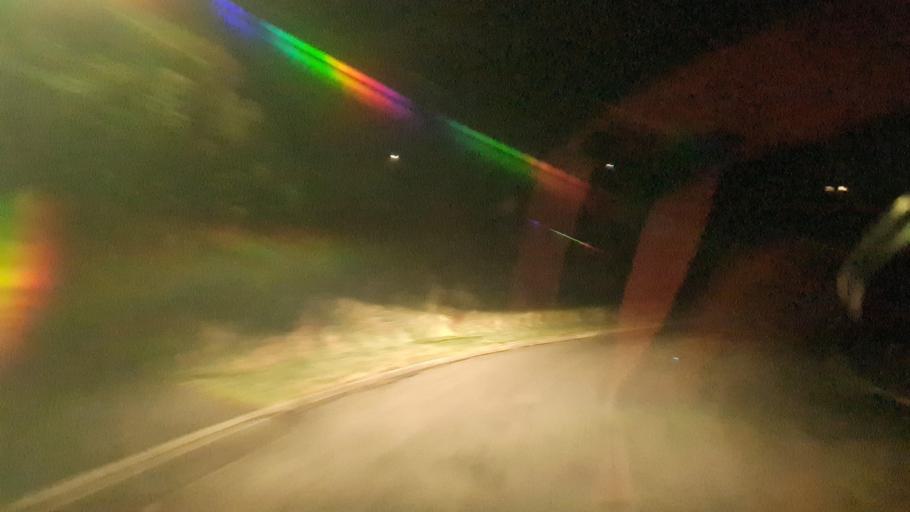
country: NZ
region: Otago
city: Oamaru
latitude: -45.0795
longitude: 170.9713
